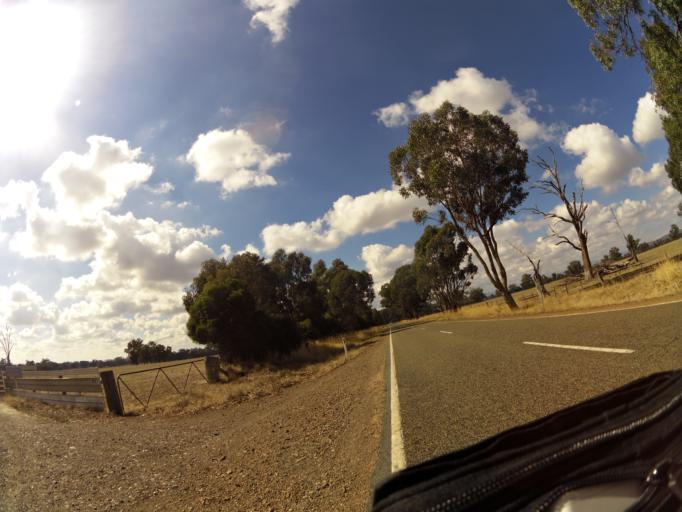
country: AU
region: Victoria
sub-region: Benalla
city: Benalla
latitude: -36.6094
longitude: 146.0185
